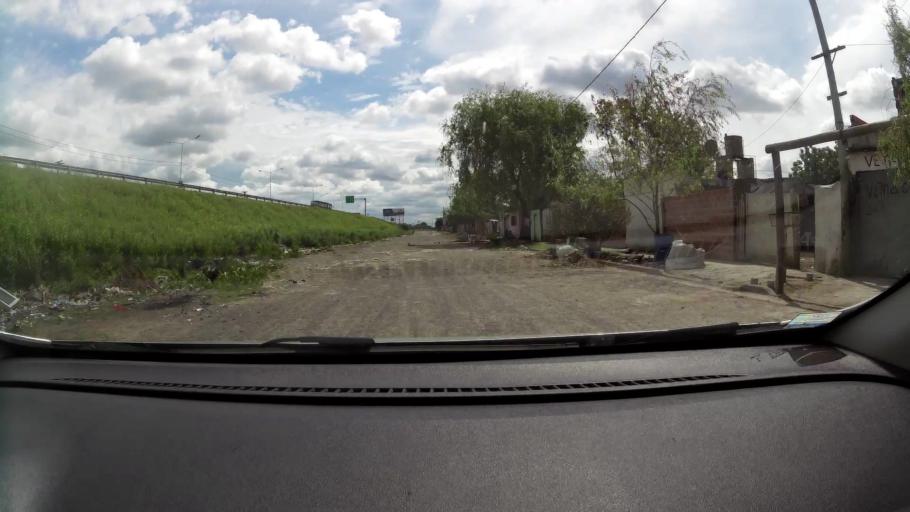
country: AR
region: Santa Fe
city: Gobernador Galvez
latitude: -33.0158
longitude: -60.6430
